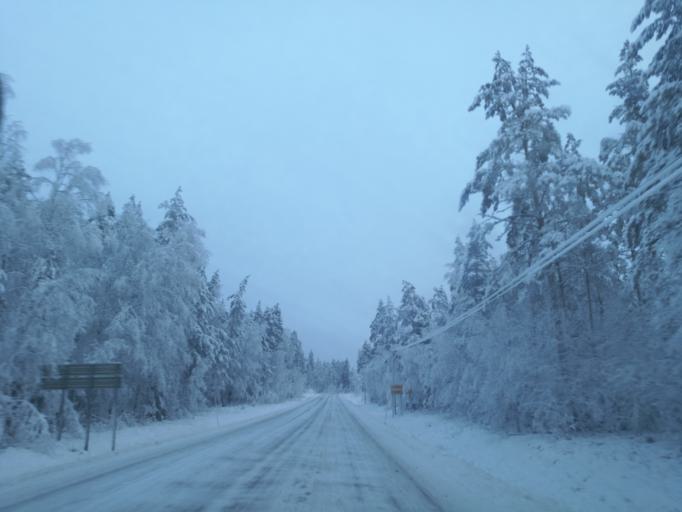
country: NO
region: Hedmark
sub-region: Grue
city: Kirkenaer
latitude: 60.3965
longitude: 12.3693
